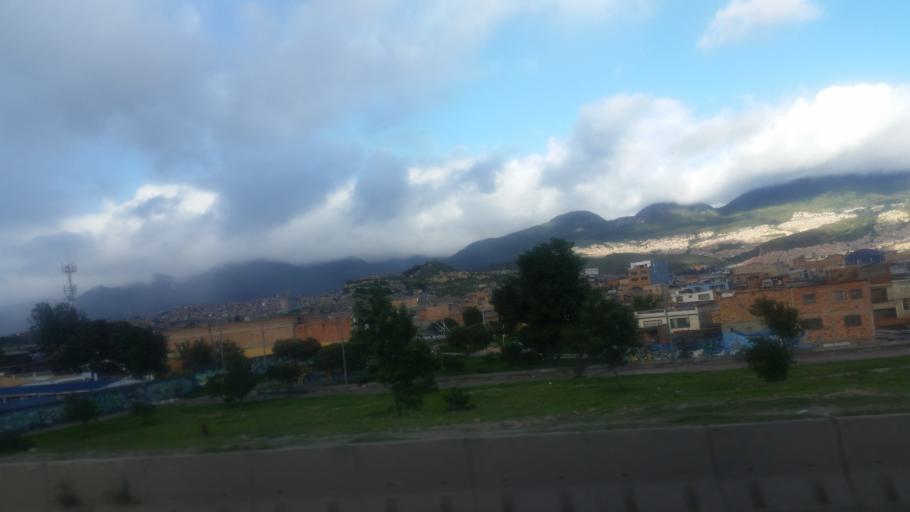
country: CO
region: Bogota D.C.
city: Bogota
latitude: 4.5659
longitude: -74.1381
